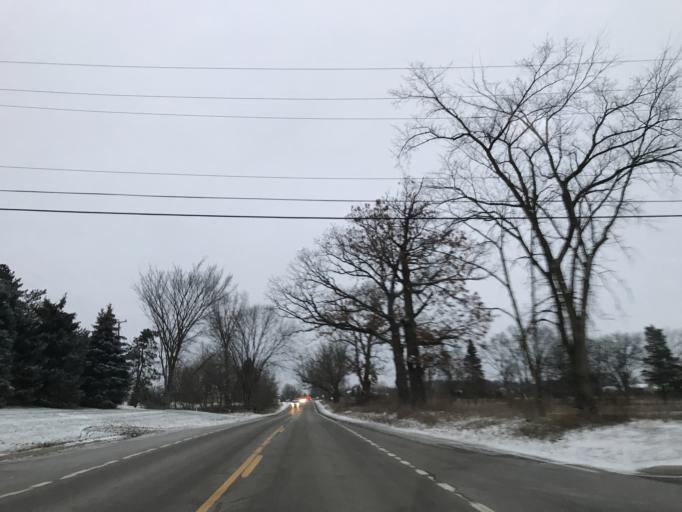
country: US
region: Michigan
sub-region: Oakland County
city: South Lyon
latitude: 42.4359
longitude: -83.6496
